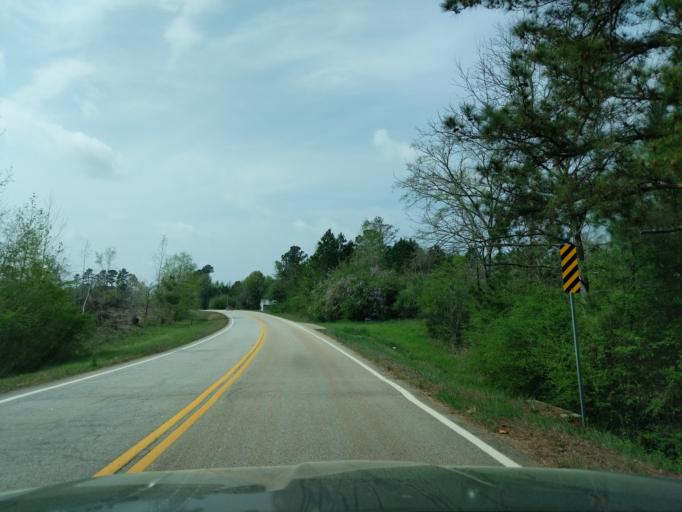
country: US
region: Georgia
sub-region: Lincoln County
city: Lincolnton
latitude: 33.7709
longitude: -82.3739
